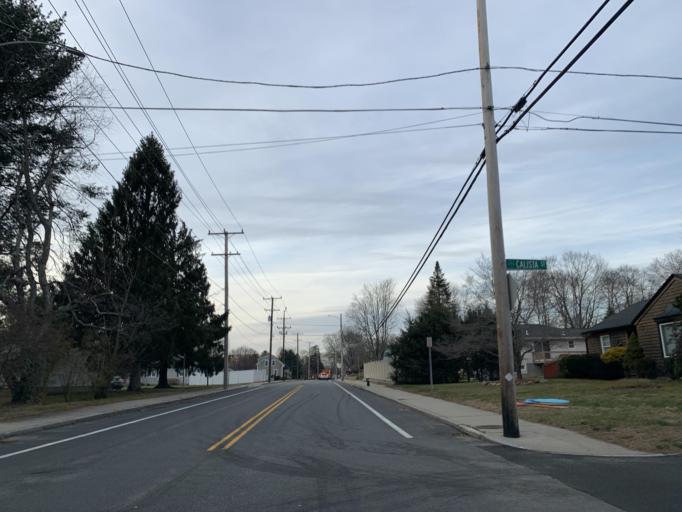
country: US
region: Rhode Island
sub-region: Providence County
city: Greenville
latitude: 41.8659
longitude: -71.5464
